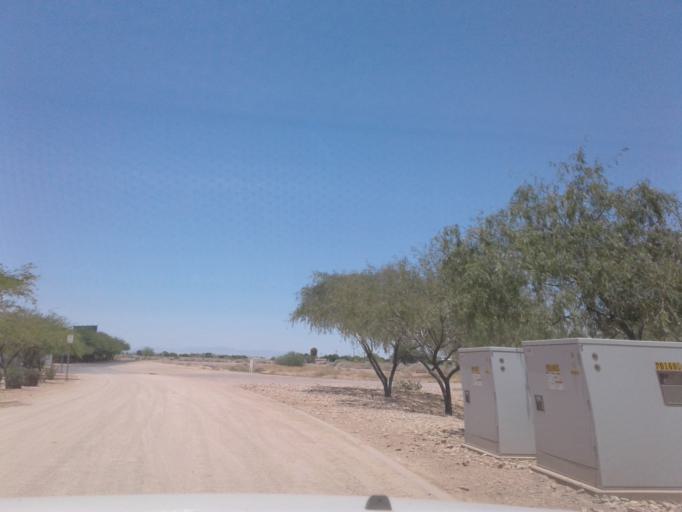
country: US
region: Arizona
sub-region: Maricopa County
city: Tolleson
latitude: 33.5115
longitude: -112.2905
